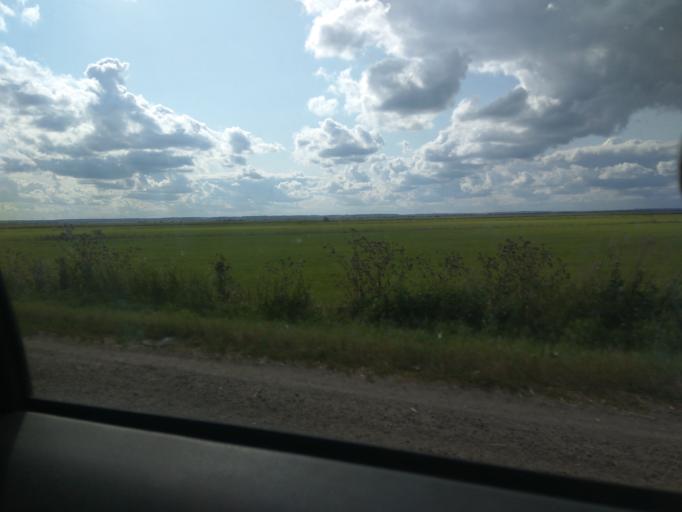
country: RU
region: Moskovskaya
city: Ramenskoye
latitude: 55.5229
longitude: 38.2768
